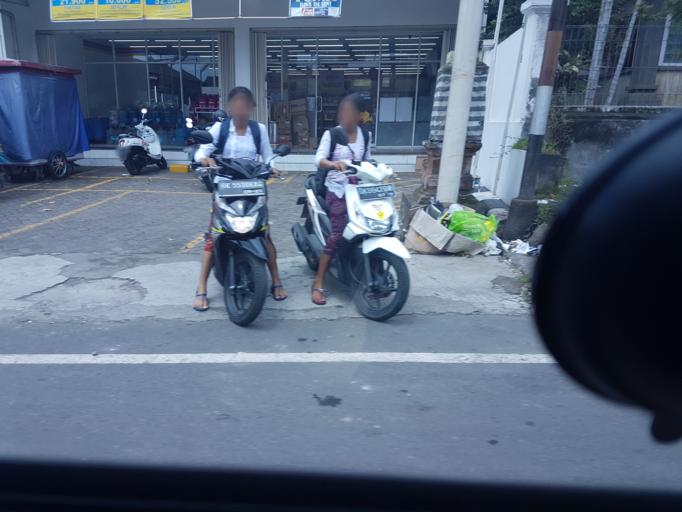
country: ID
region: Bali
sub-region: Kabupaten Gianyar
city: Ubud
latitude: -8.5146
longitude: 115.2935
